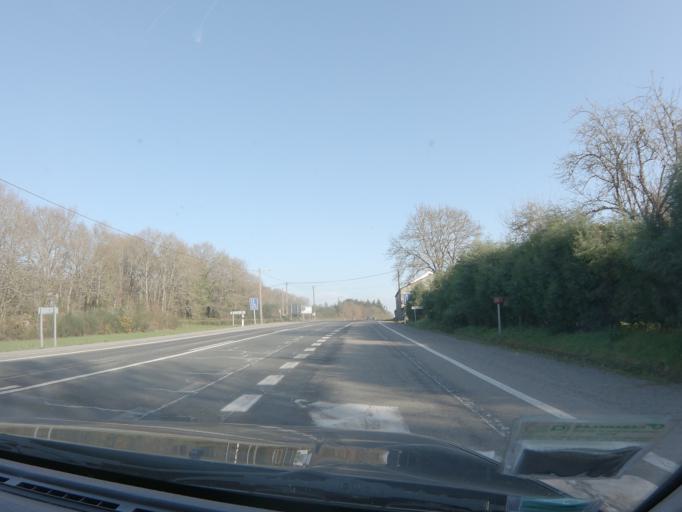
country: ES
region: Galicia
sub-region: Provincia de Lugo
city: Corgo
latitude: 42.9551
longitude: -7.4657
